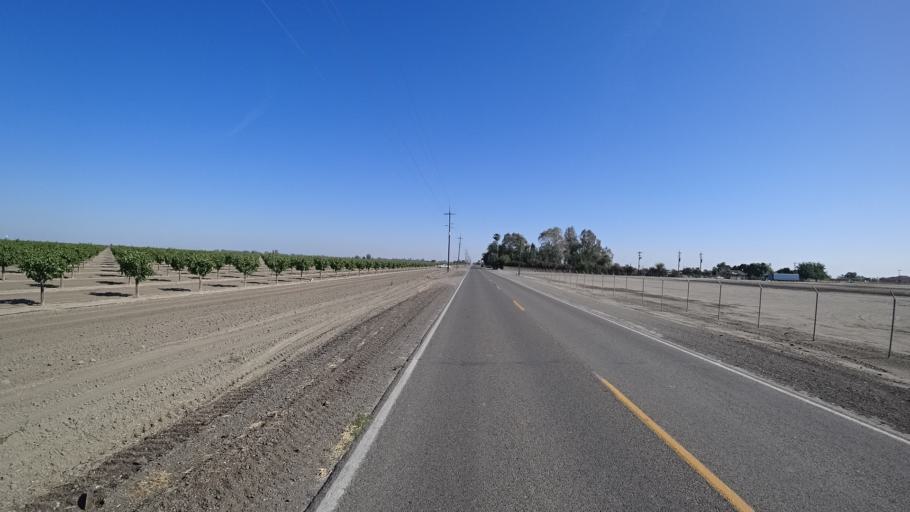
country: US
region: California
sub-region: Kings County
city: Corcoran
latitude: 36.0711
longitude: -119.5720
